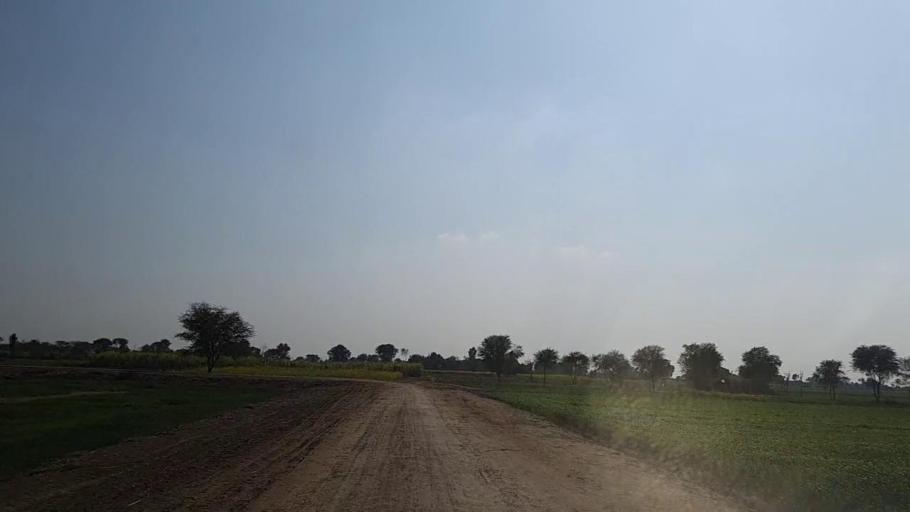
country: PK
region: Sindh
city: Daur
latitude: 26.4310
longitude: 68.2344
